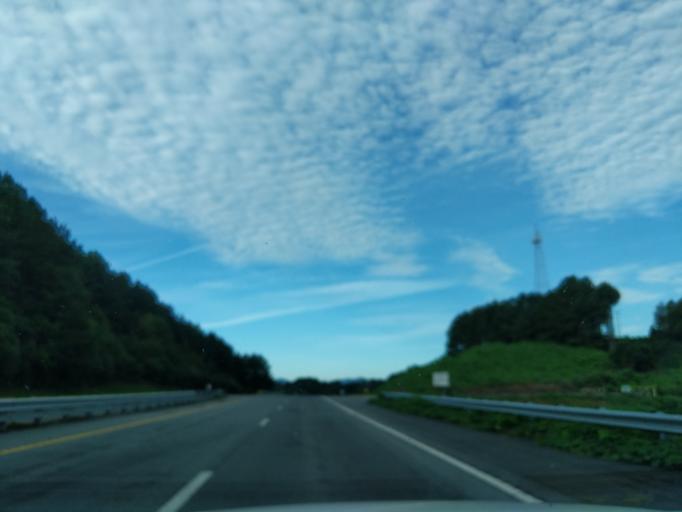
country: US
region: Georgia
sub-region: Fannin County
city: McCaysville
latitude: 35.0079
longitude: -84.3844
